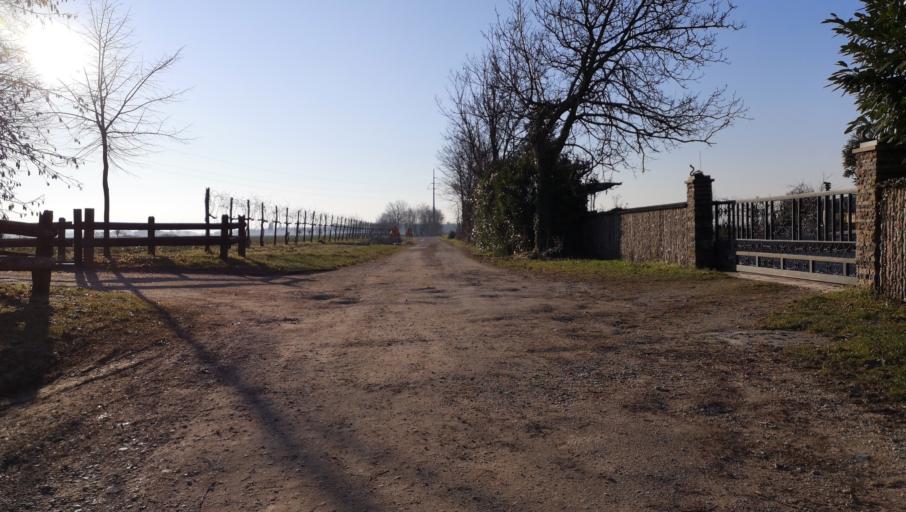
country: IT
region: Friuli Venezia Giulia
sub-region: Provincia di Udine
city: Lauzacco
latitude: 45.9774
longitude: 13.2903
